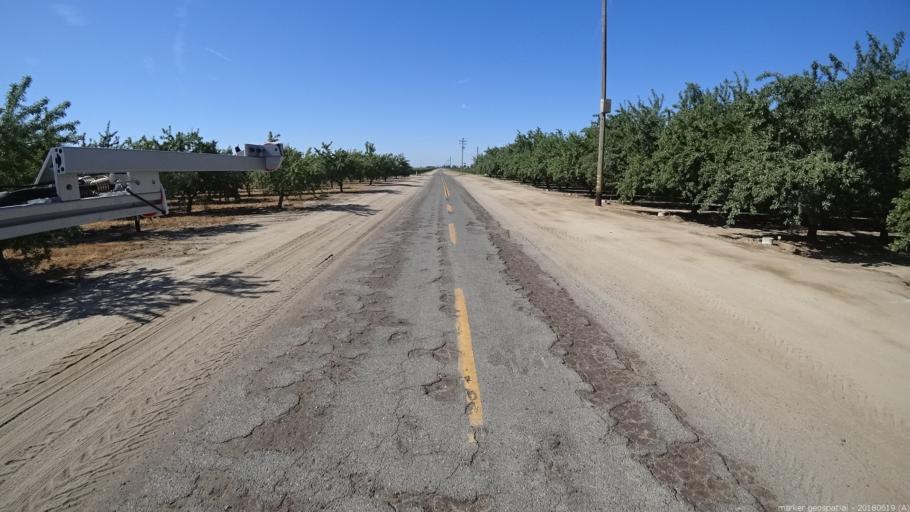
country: US
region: California
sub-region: Fresno County
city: Biola
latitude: 36.8306
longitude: -120.0427
